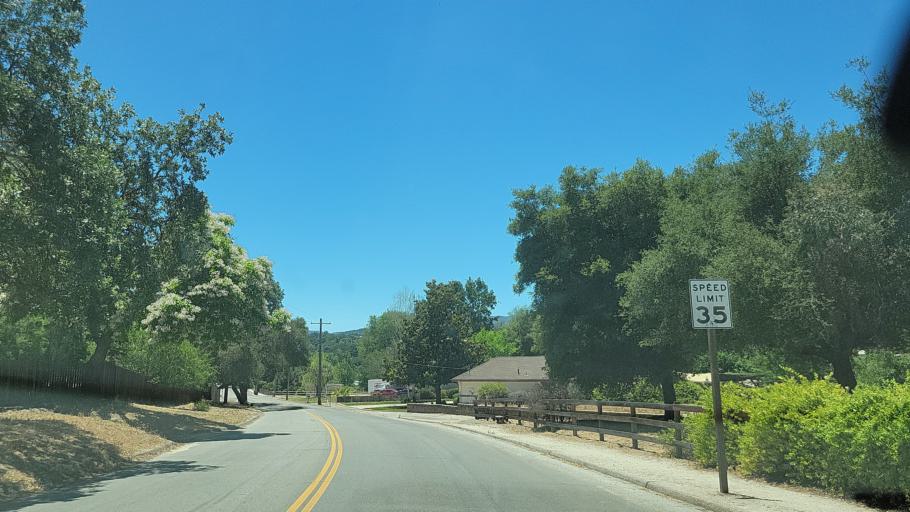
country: US
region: California
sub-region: San Luis Obispo County
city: Atascadero
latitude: 35.5033
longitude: -120.6827
